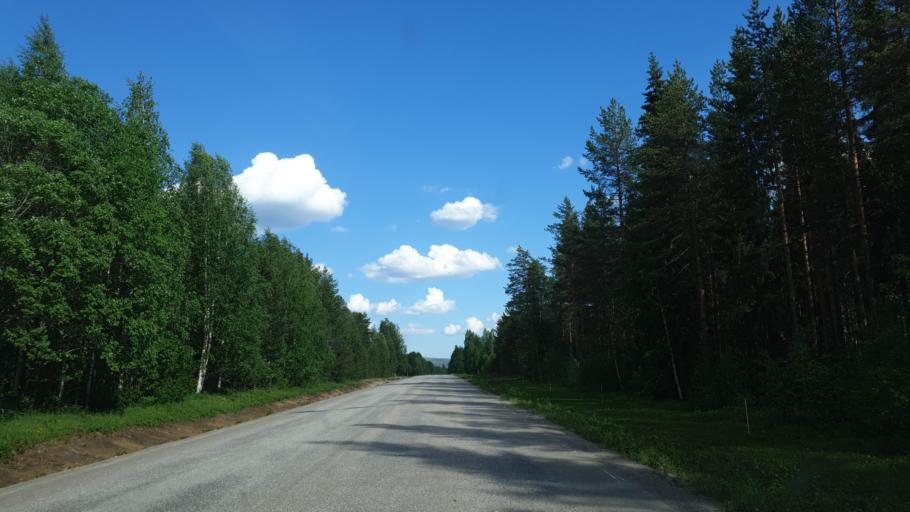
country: SE
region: Norrbotten
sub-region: Alvsbyns Kommun
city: AElvsbyn
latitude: 65.8471
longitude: 20.4674
